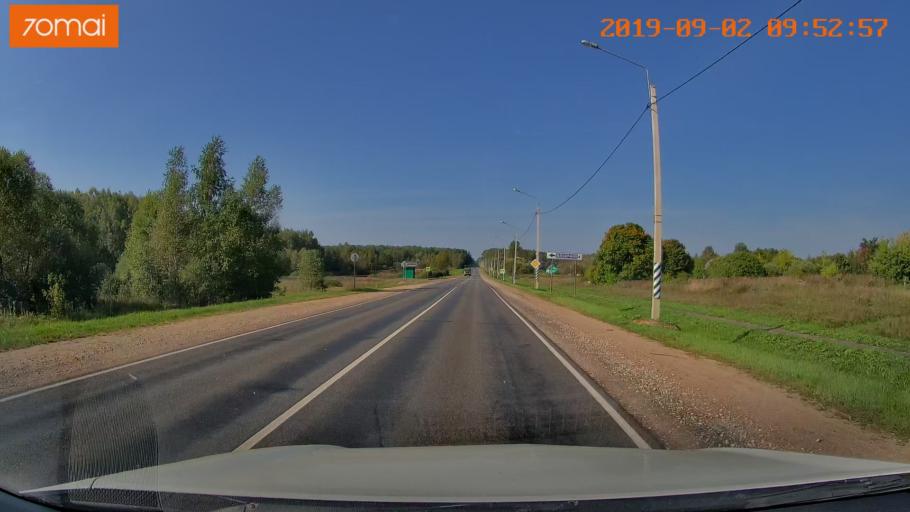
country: RU
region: Kaluga
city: Mosal'sk
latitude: 54.5867
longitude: 34.6831
